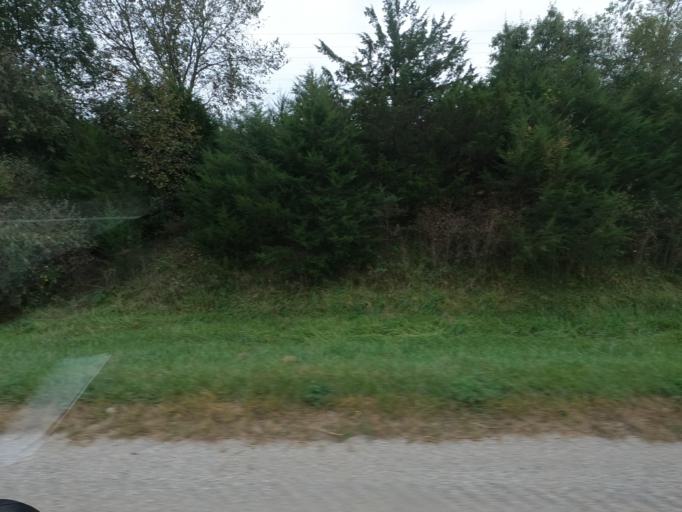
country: US
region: Iowa
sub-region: Van Buren County
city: Keosauqua
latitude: 40.8349
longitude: -91.9691
